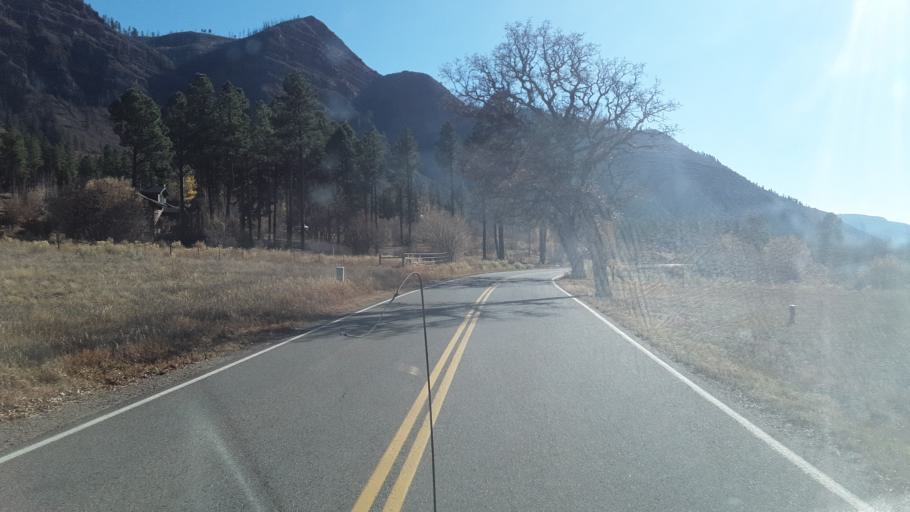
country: US
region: Colorado
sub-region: La Plata County
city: Durango
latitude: 37.4078
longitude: -107.8137
